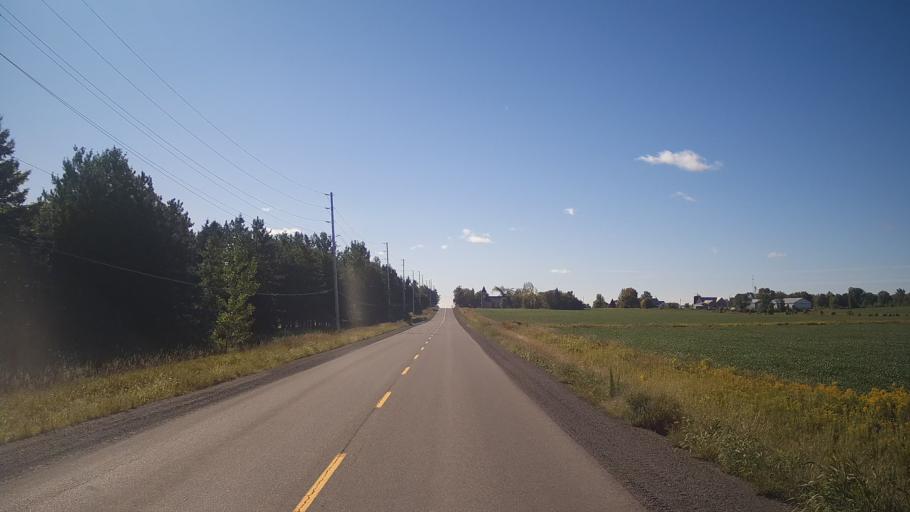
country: CA
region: Ontario
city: Prescott
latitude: 44.9744
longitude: -75.5357
